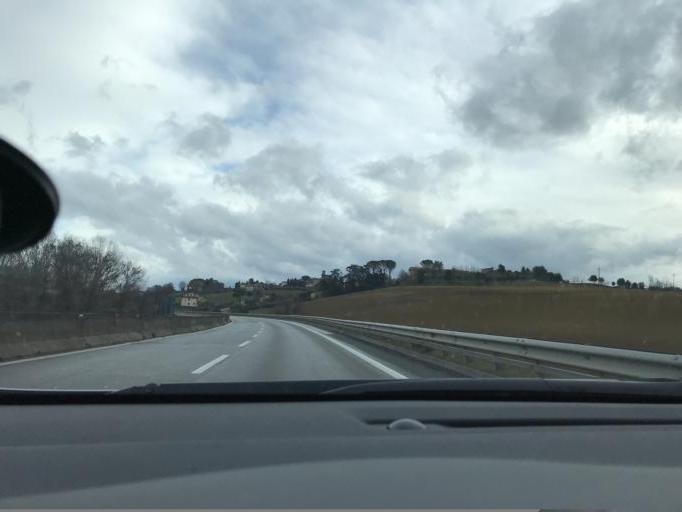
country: IT
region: Umbria
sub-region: Provincia di Perugia
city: Via Lippia
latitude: 43.1026
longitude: 12.4807
